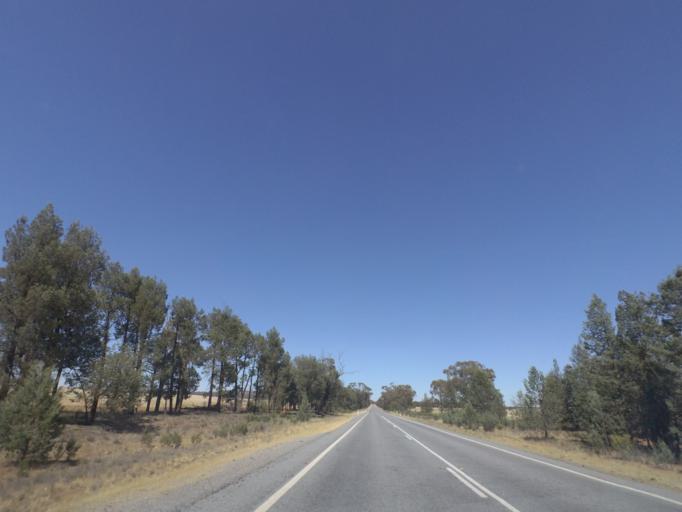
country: AU
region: New South Wales
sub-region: Narrandera
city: Narrandera
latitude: -34.4147
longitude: 146.8634
